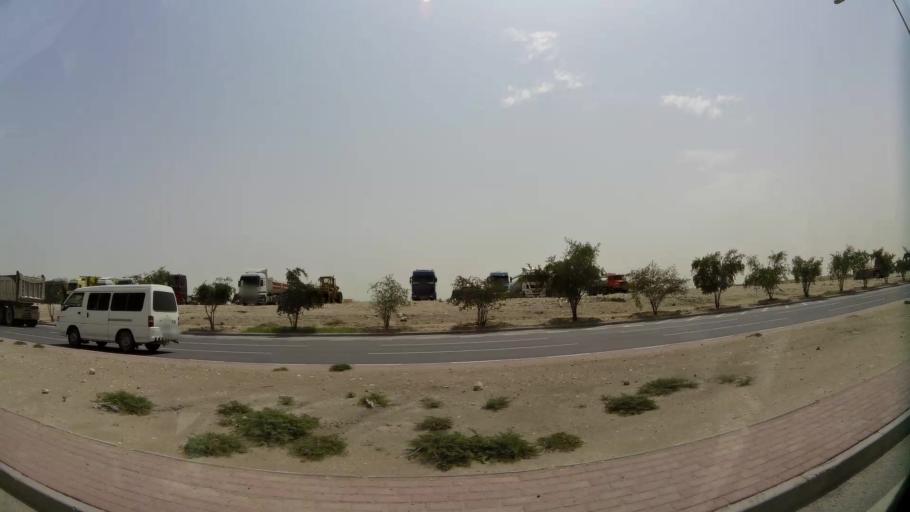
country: QA
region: Baladiyat ar Rayyan
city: Ar Rayyan
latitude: 25.2430
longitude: 51.4149
